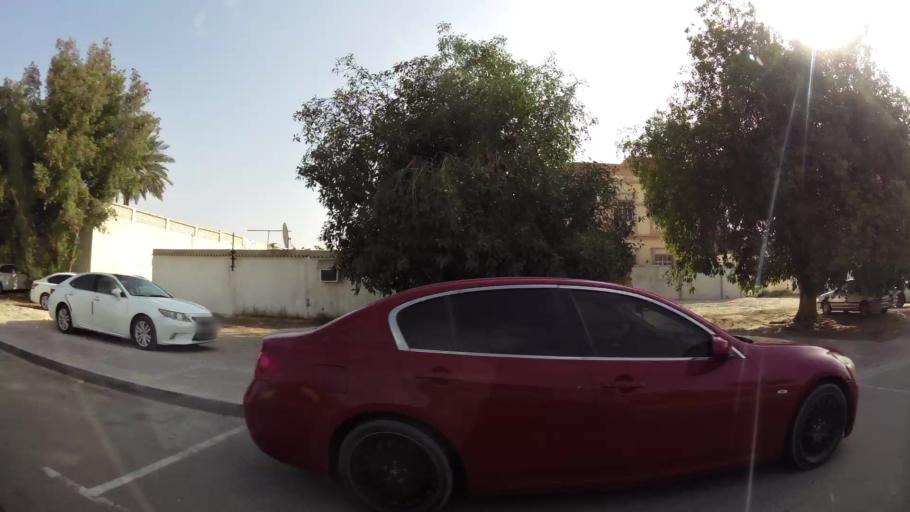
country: AE
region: Ash Shariqah
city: Sharjah
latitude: 25.2245
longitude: 55.3799
